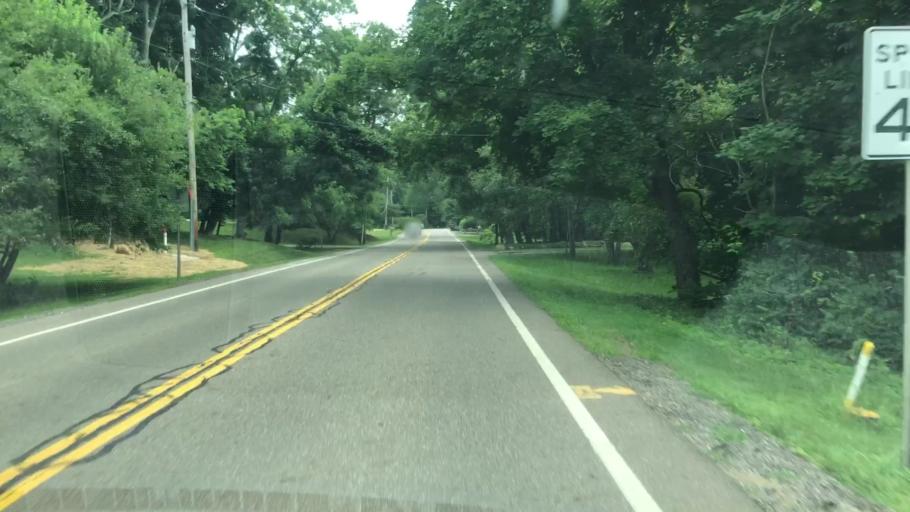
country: US
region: Ohio
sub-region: Summit County
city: Montrose-Ghent
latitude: 41.1569
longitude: -81.6220
